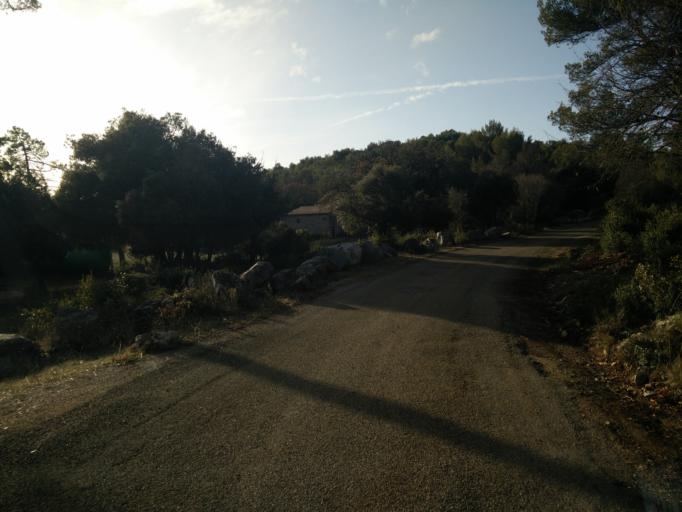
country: FR
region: Provence-Alpes-Cote d'Azur
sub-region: Departement du Var
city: Signes
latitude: 43.2372
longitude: 5.8901
